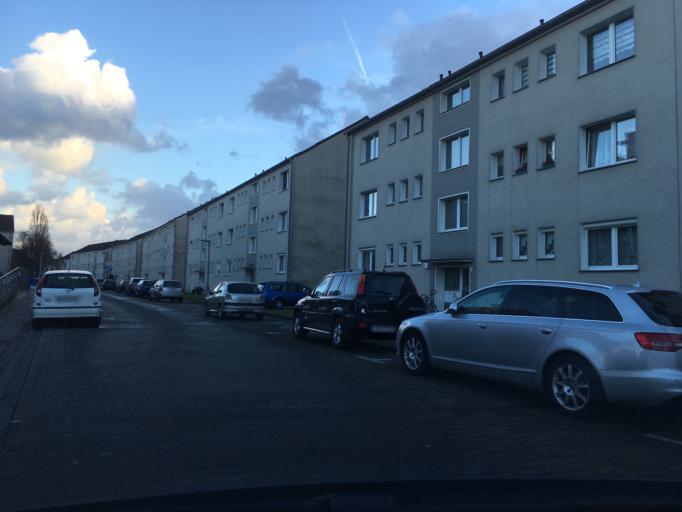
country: DE
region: North Rhine-Westphalia
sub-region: Regierungsbezirk Dusseldorf
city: Oberhausen
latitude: 51.4772
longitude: 6.8821
